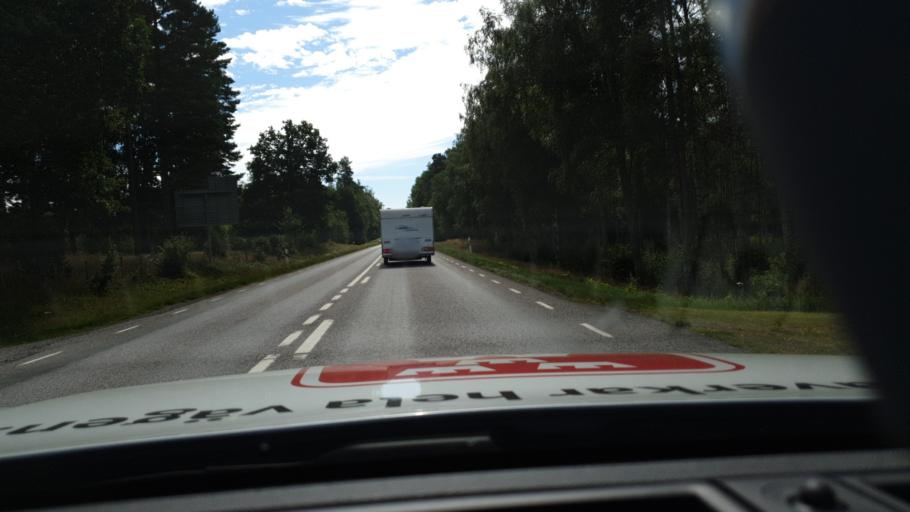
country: SE
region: Kronoberg
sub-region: Vaxjo Kommun
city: Lammhult
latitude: 57.1904
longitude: 14.5362
